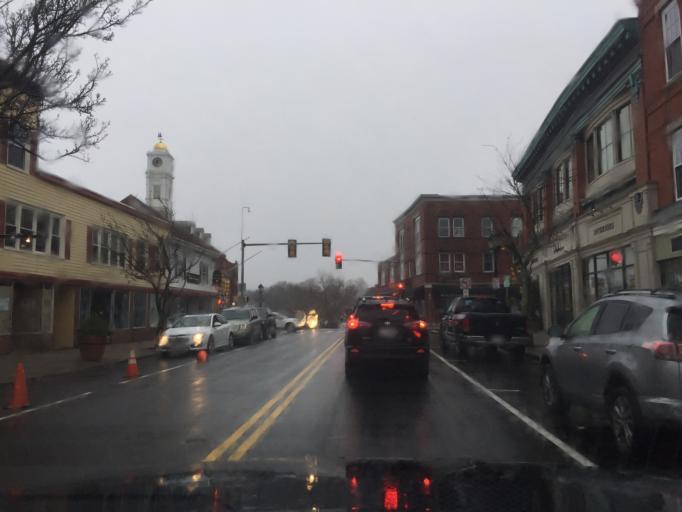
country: US
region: Massachusetts
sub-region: Plymouth County
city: Plymouth
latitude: 41.9562
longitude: -70.6643
